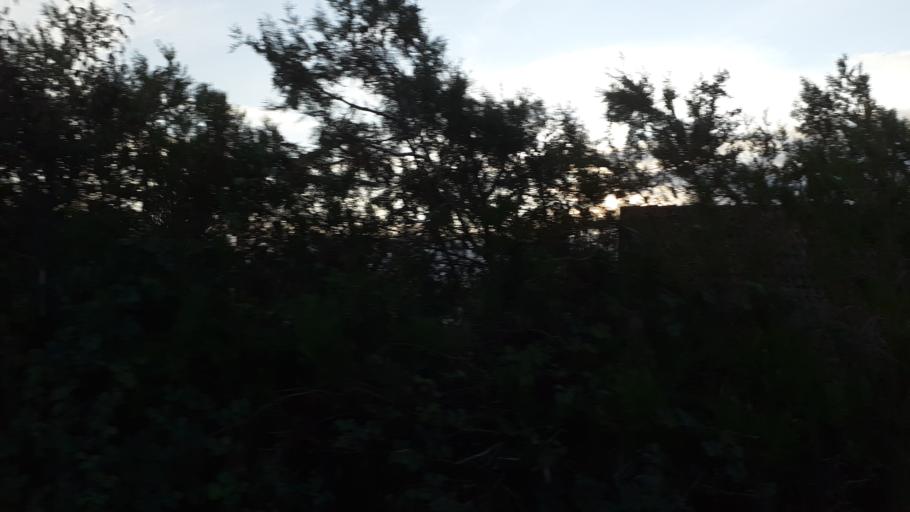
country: FR
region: Franche-Comte
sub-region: Departement du Doubs
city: Novillars
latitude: 47.2875
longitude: 6.1465
